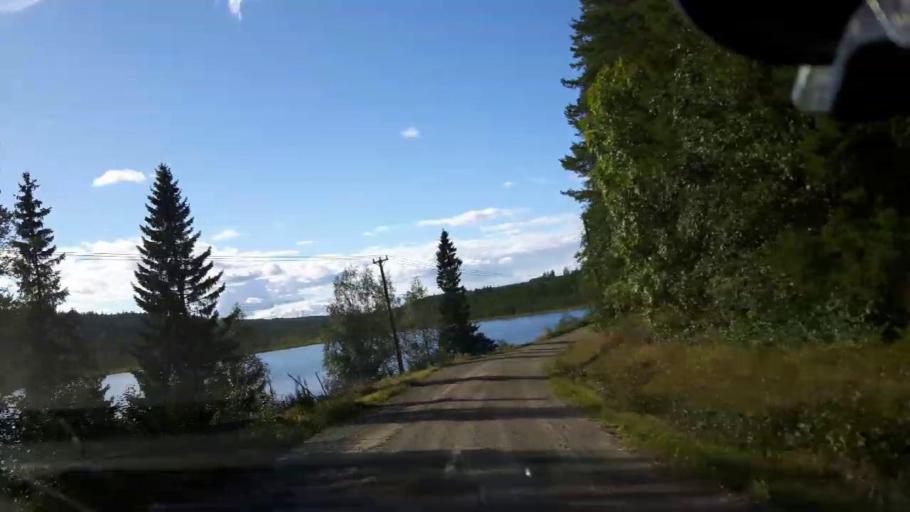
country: SE
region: Jaemtland
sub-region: Ragunda Kommun
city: Hammarstrand
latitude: 63.4767
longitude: 16.1555
